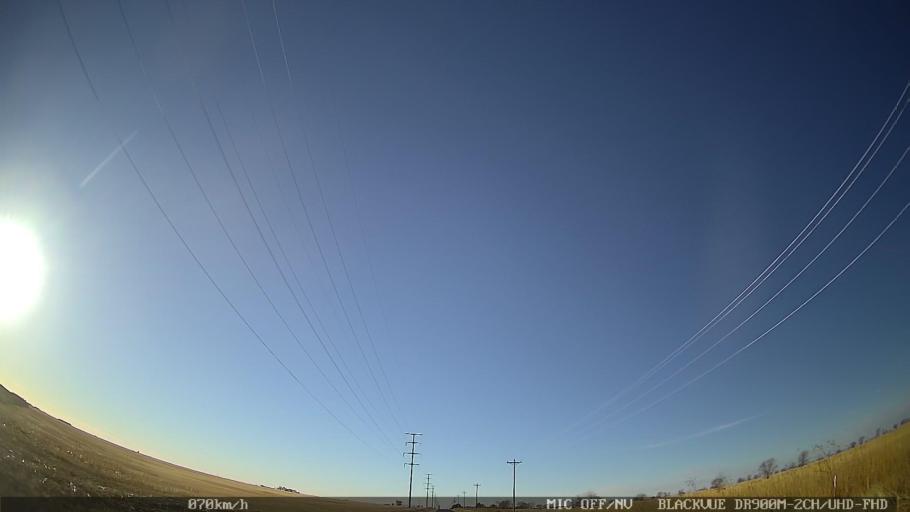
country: US
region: New Mexico
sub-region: Curry County
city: Clovis
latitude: 34.4303
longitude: -103.2493
